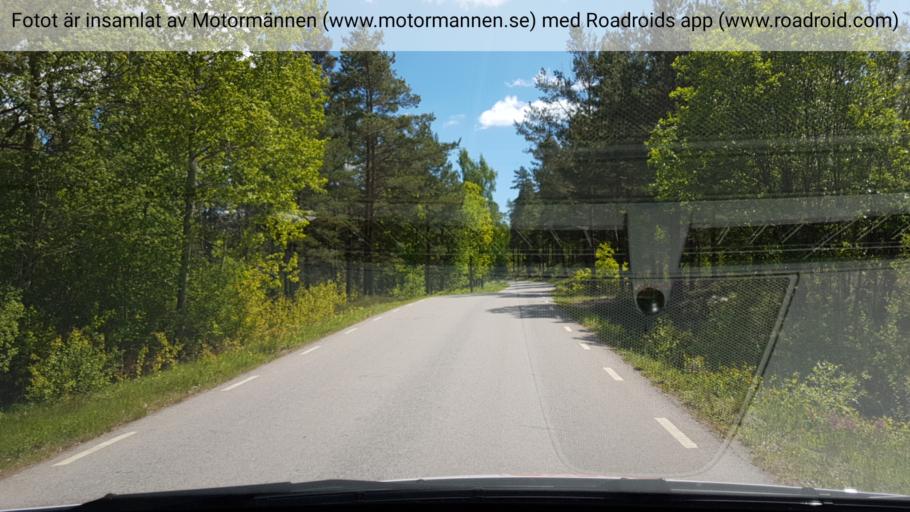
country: SE
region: Kalmar
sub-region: Vasterviks Kommun
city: Vaestervik
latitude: 57.9370
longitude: 16.6725
